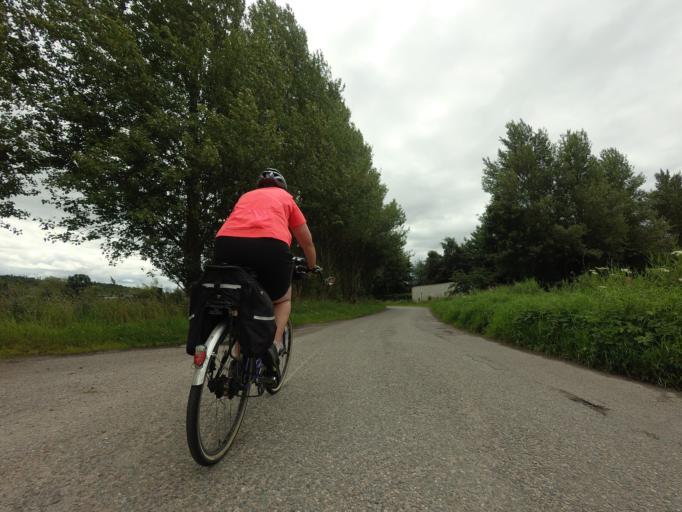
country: GB
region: Scotland
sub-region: Moray
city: Forres
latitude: 57.6157
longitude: -3.6197
